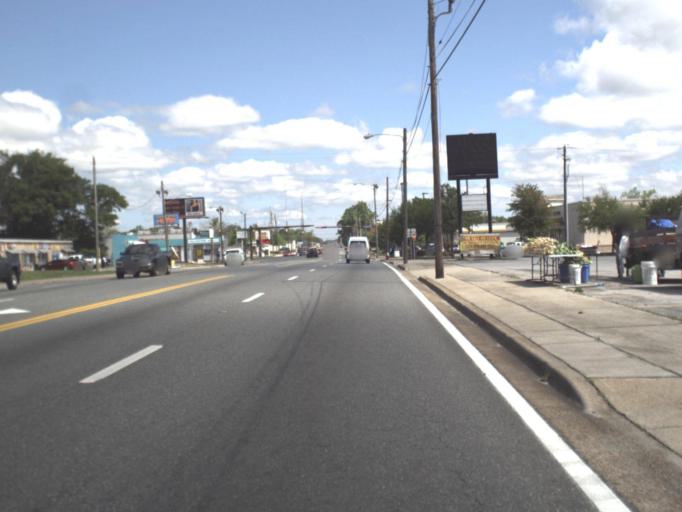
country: US
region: Florida
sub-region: Escambia County
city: Pensacola
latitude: 30.4188
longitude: -87.2413
